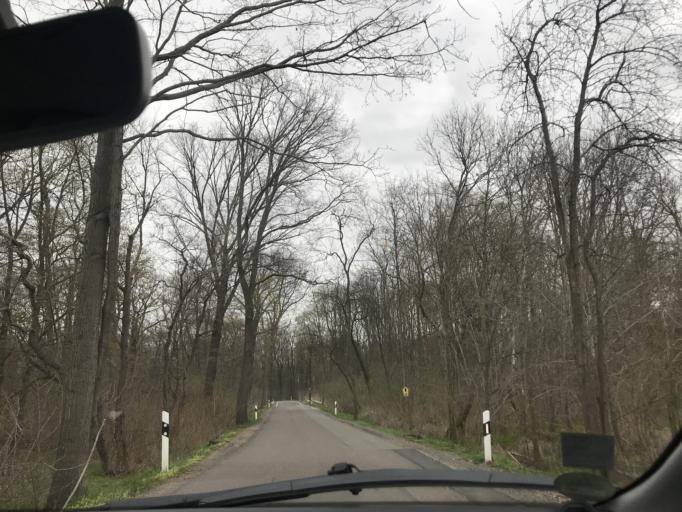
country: DE
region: Saxony
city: Schkeuditz
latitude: 51.3763
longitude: 12.2654
